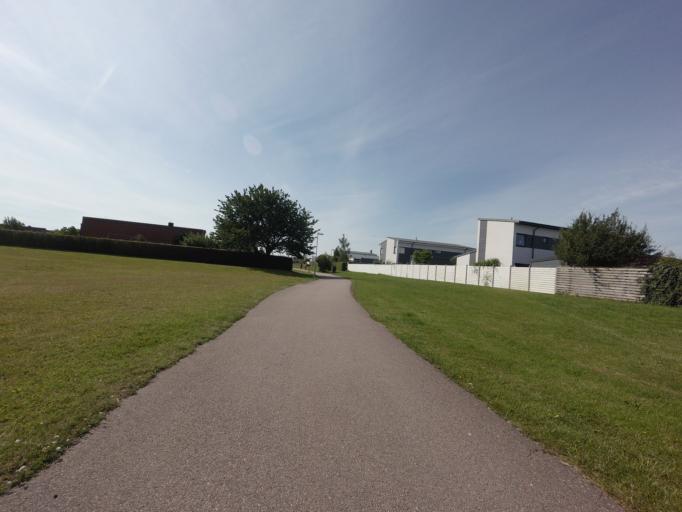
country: SE
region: Skane
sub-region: Helsingborg
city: Glumslov
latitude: 55.9484
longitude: 12.8024
